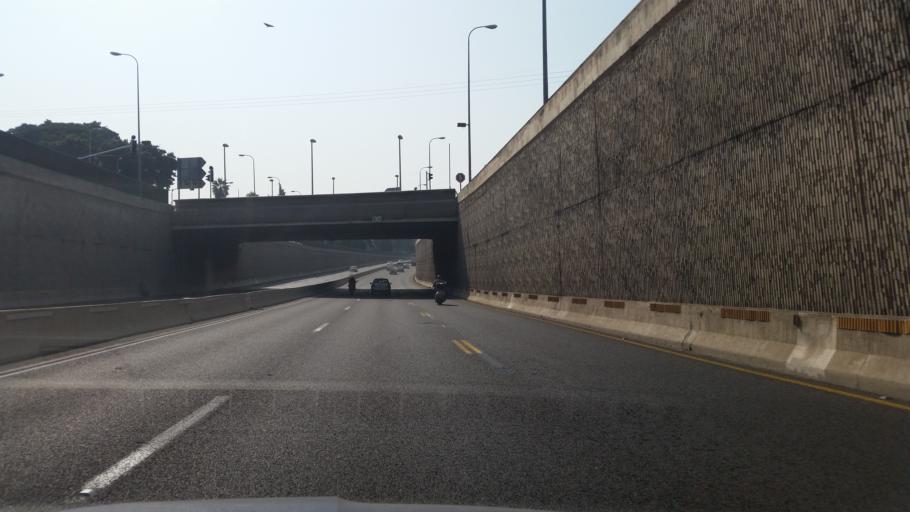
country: IL
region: Tel Aviv
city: Kefar Shemaryahu
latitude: 32.1800
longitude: 34.8159
